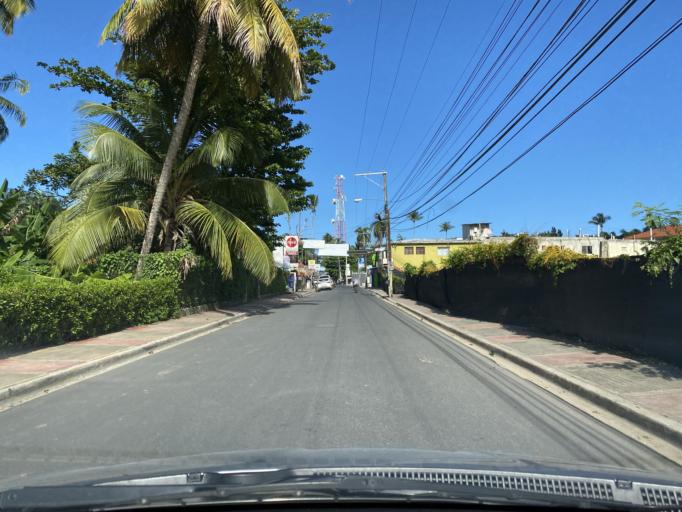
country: DO
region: Samana
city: Las Terrenas
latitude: 19.3186
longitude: -69.5395
